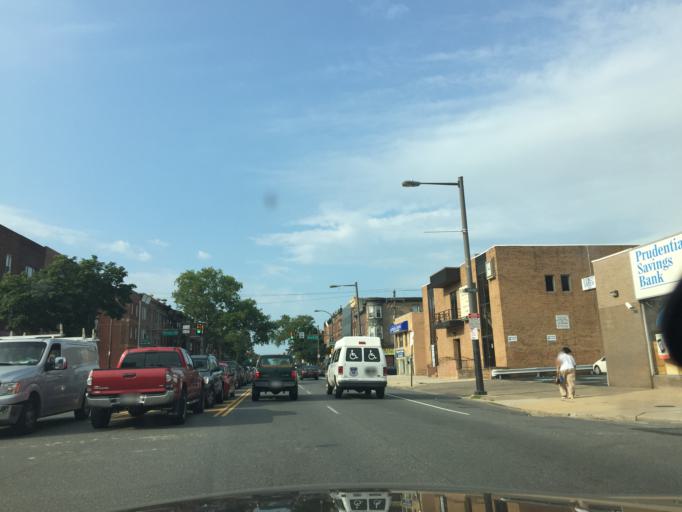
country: US
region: Pennsylvania
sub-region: Philadelphia County
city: Philadelphia
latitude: 39.9288
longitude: -75.1688
